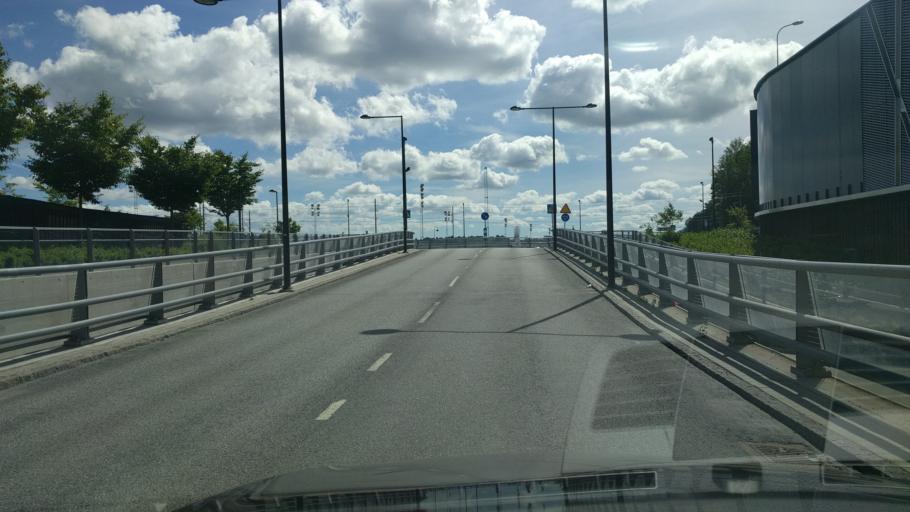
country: SE
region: Stockholm
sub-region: Taby Kommun
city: Taby
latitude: 59.4455
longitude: 18.0747
